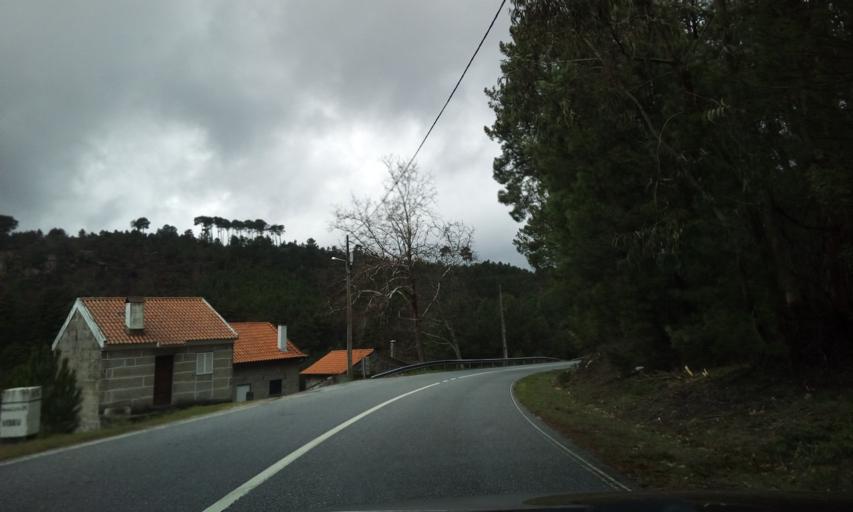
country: PT
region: Guarda
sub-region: Fornos de Algodres
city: Fornos de Algodres
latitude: 40.6089
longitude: -7.5754
